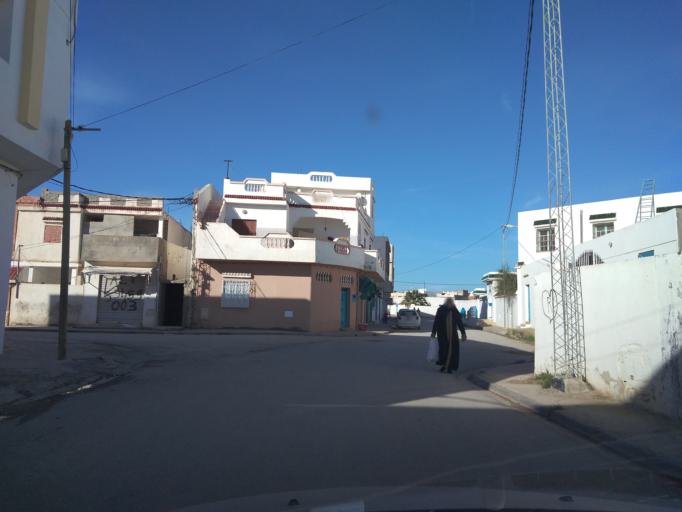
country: TN
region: Ariana
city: Qal'at al Andalus
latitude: 37.0606
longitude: 10.1206
